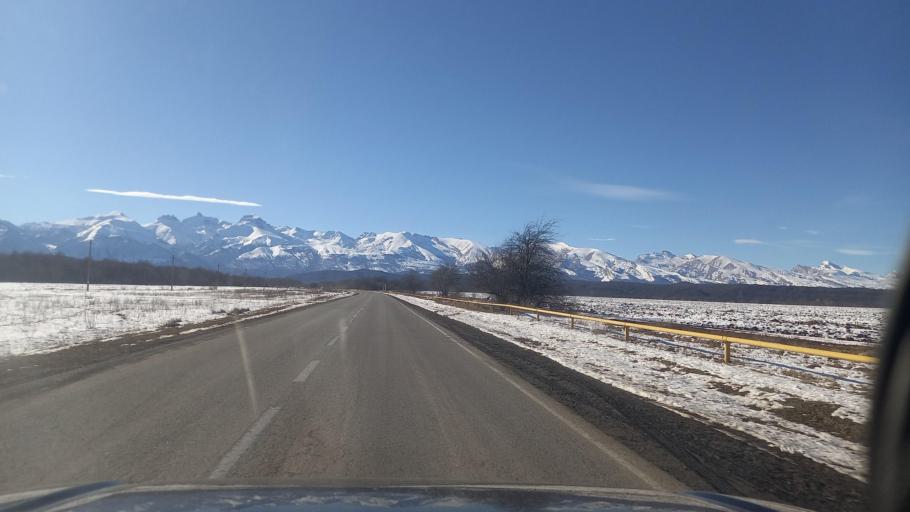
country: RU
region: North Ossetia
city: Chikola
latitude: 43.1704
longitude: 43.8671
